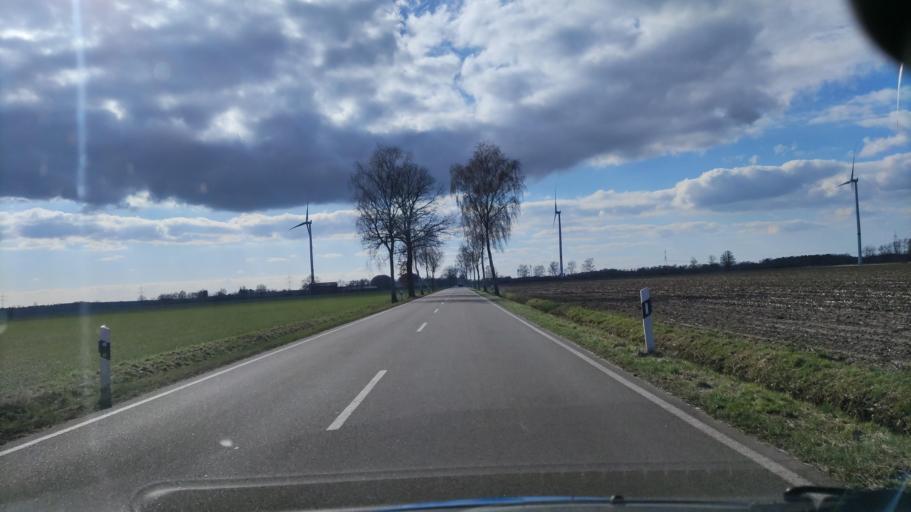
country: DE
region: Lower Saxony
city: Beedenbostel
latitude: 52.6601
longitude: 10.2835
